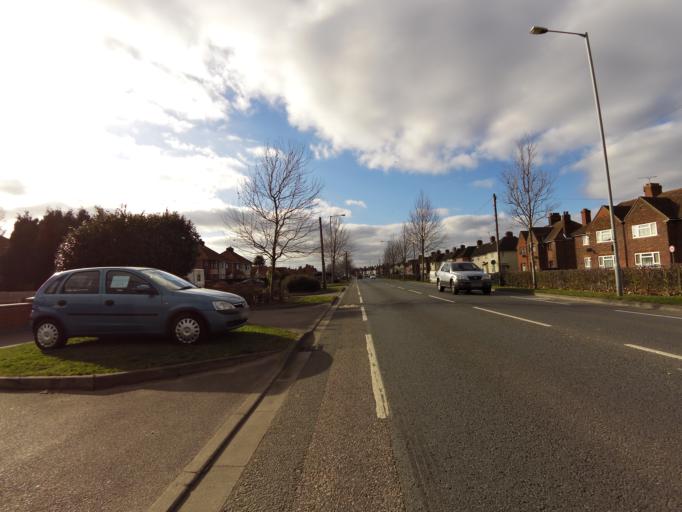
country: GB
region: England
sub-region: Suffolk
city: Ipswich
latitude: 52.0341
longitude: 1.1954
